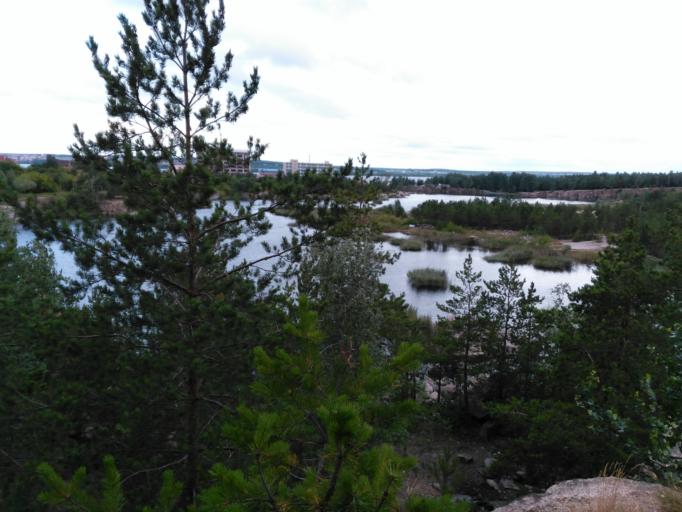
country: RU
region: Chelyabinsk
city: Novosineglazovskiy
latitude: 55.1223
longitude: 61.3389
